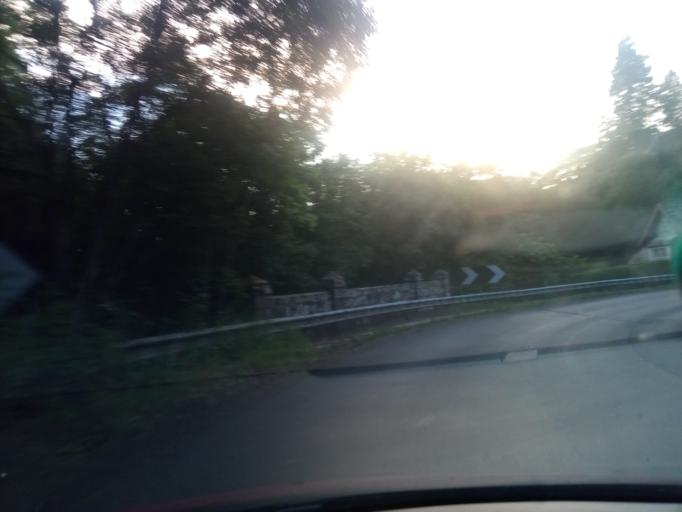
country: GB
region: England
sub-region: Northumberland
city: Bardon Mill
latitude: 54.8927
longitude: -2.3528
